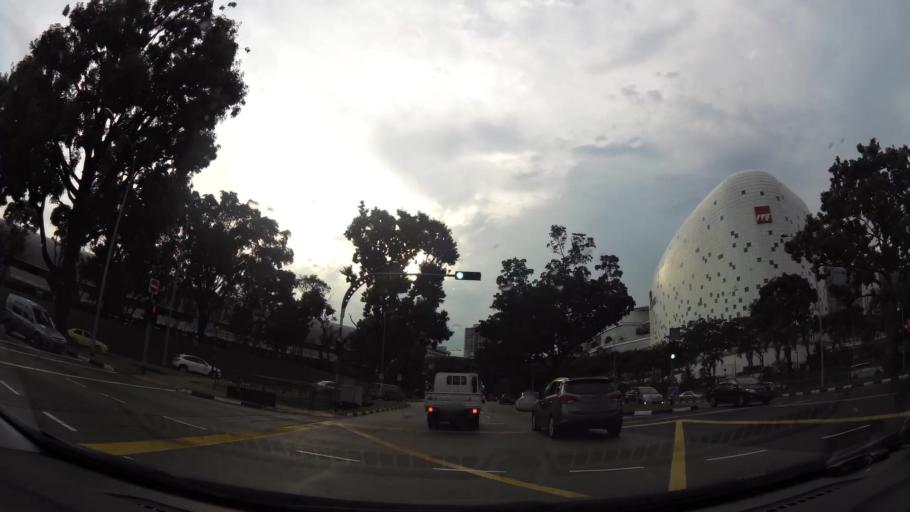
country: SG
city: Singapore
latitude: 1.3764
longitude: 103.8582
